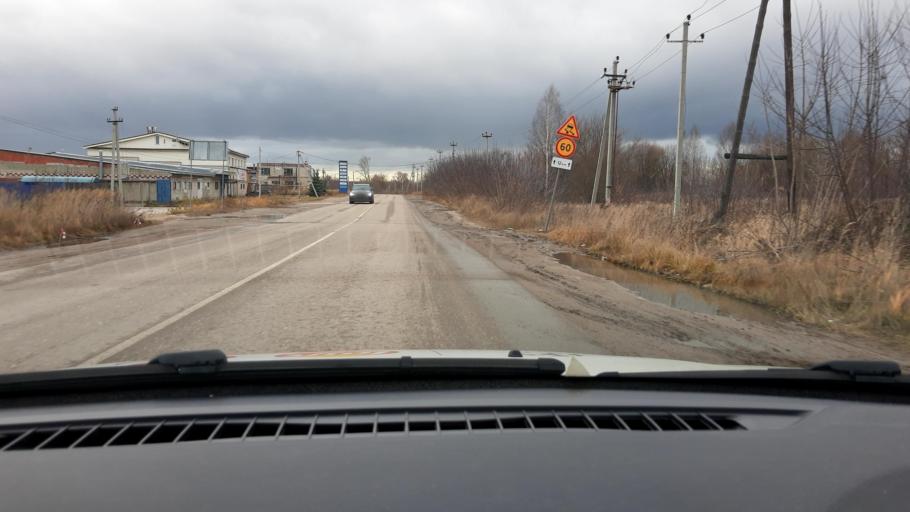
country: RU
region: Nizjnij Novgorod
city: Bogorodsk
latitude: 56.1158
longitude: 43.5276
